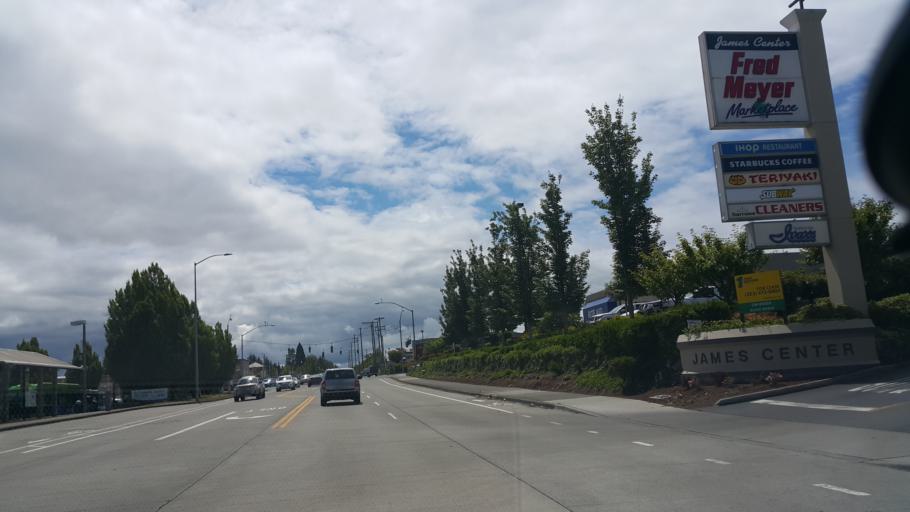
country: US
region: Washington
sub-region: Pierce County
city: Fircrest
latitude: 47.2441
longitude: -122.5264
